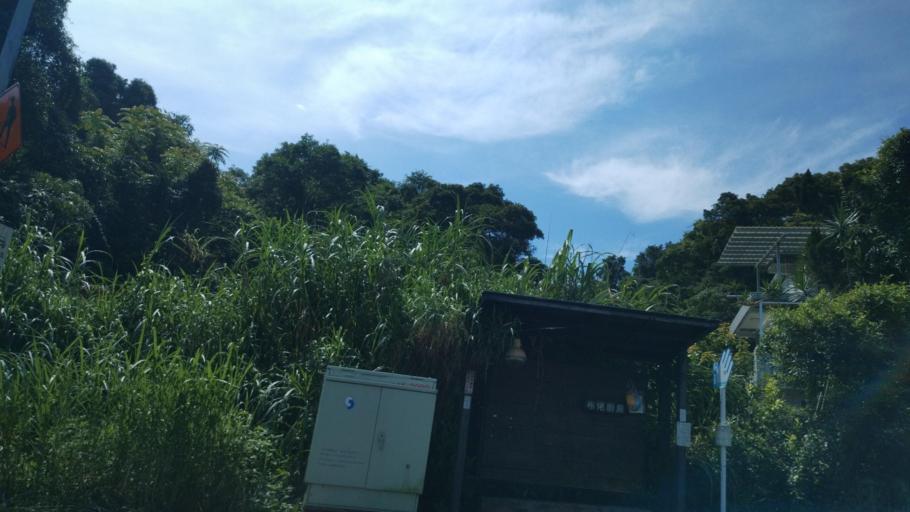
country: TW
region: Taipei
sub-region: Taipei
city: Banqiao
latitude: 24.9490
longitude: 121.5052
